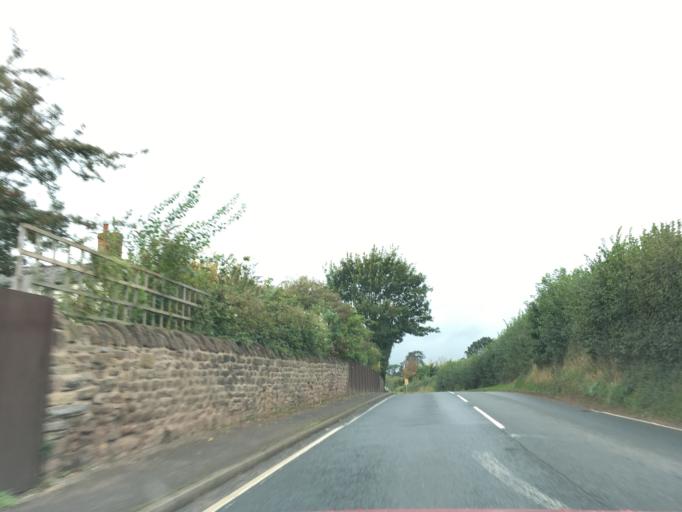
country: GB
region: England
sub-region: Herefordshire
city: Lea
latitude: 51.9042
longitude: -2.5270
